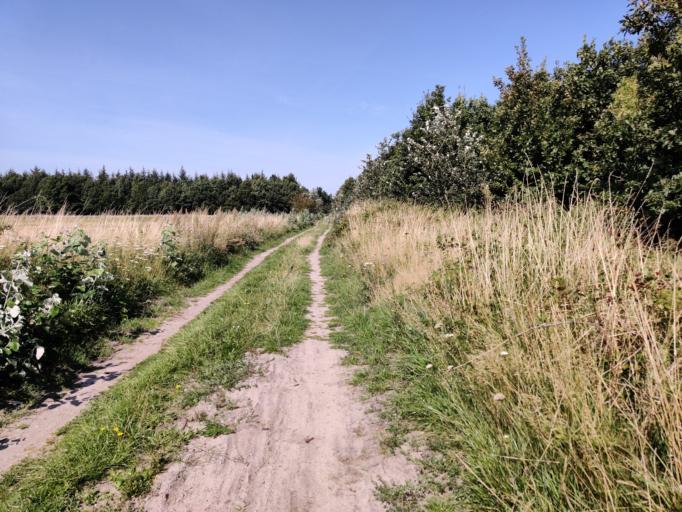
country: DK
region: Zealand
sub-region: Guldborgsund Kommune
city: Nykobing Falster
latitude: 54.6169
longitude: 11.9563
